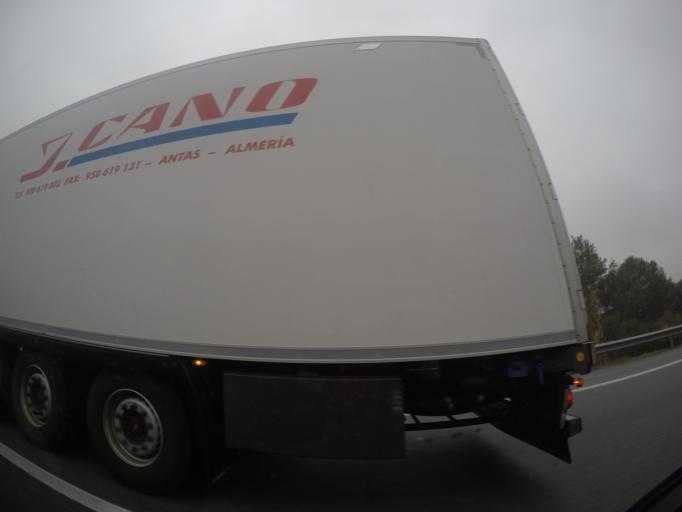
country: ES
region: Catalonia
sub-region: Provincia de Barcelona
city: Gelida
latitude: 41.4395
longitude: 1.8427
